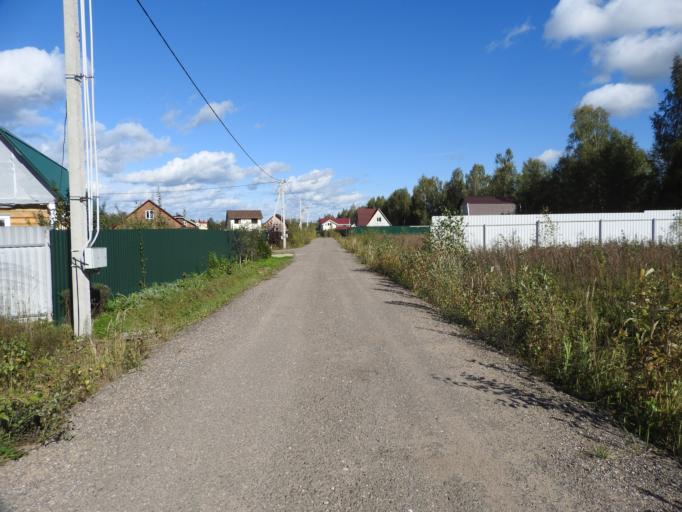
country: RU
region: Moskovskaya
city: Ruza
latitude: 55.5301
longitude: 36.2018
